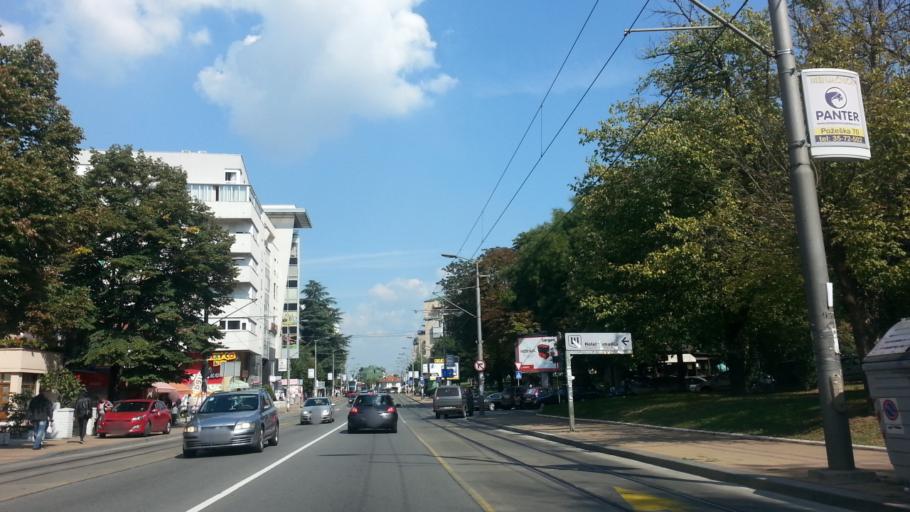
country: RS
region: Central Serbia
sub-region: Belgrade
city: Cukarica
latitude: 44.7792
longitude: 20.4160
